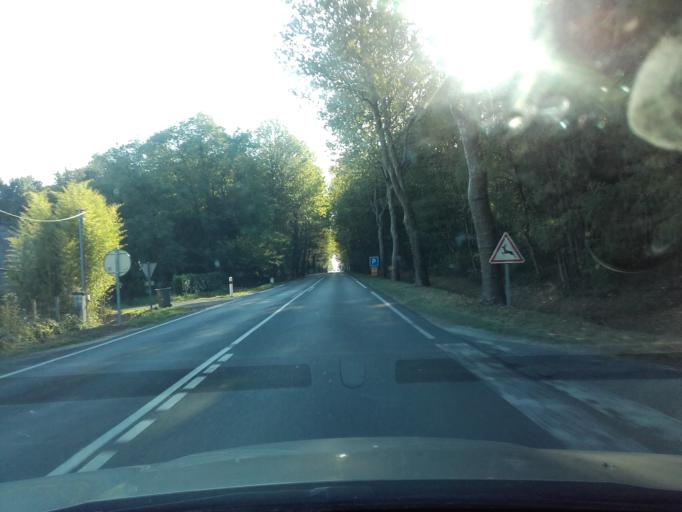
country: FR
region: Centre
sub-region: Departement d'Indre-et-Loire
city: Monnaie
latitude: 47.4901
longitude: 0.7751
